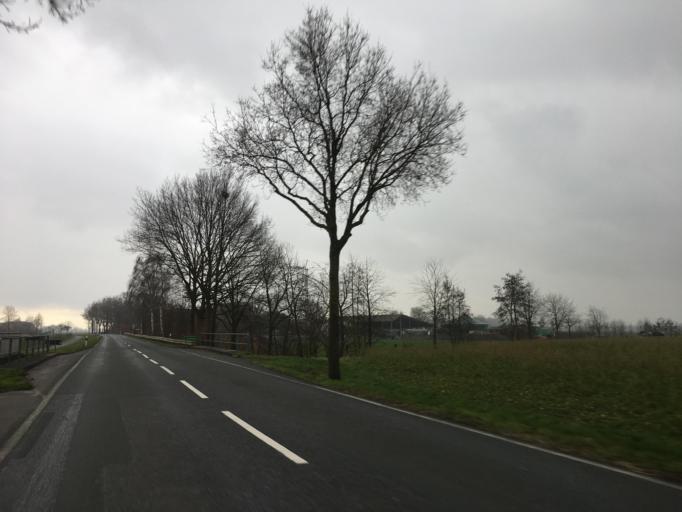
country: DE
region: North Rhine-Westphalia
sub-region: Regierungsbezirk Munster
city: Senden
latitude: 51.8583
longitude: 7.4258
